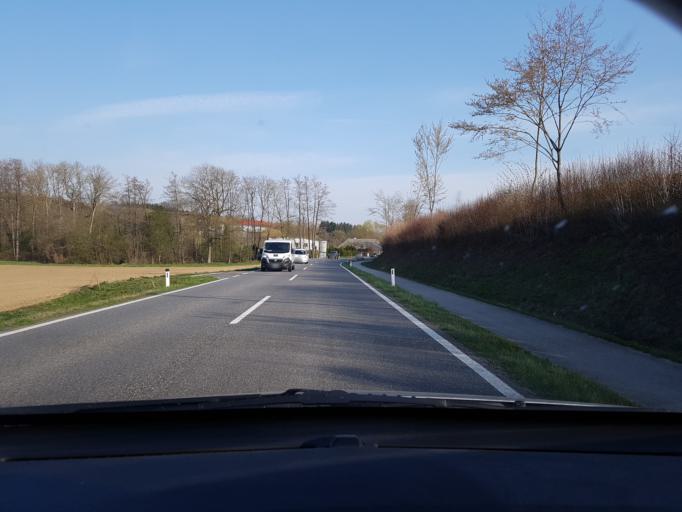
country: AT
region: Upper Austria
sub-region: Politischer Bezirk Linz-Land
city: Sankt Florian
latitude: 48.1734
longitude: 14.3433
